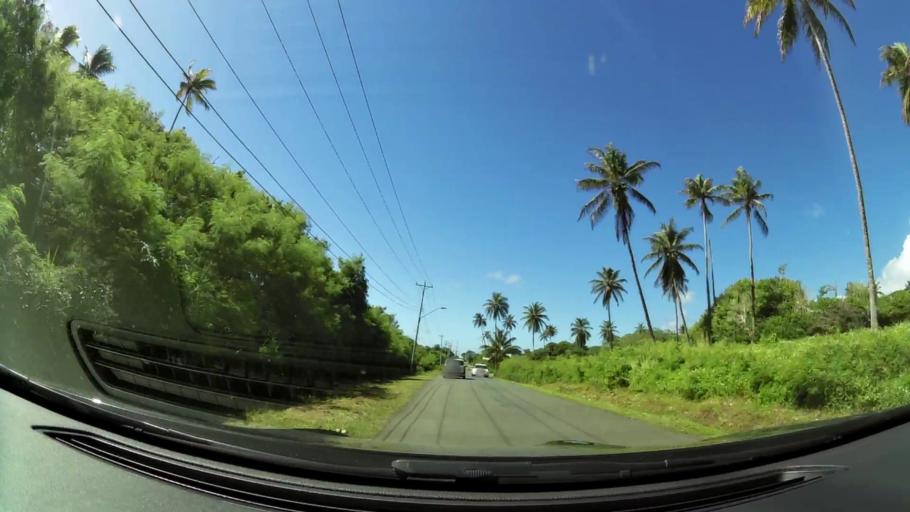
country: TT
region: Tobago
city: Scarborough
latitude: 11.1580
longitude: -60.7711
